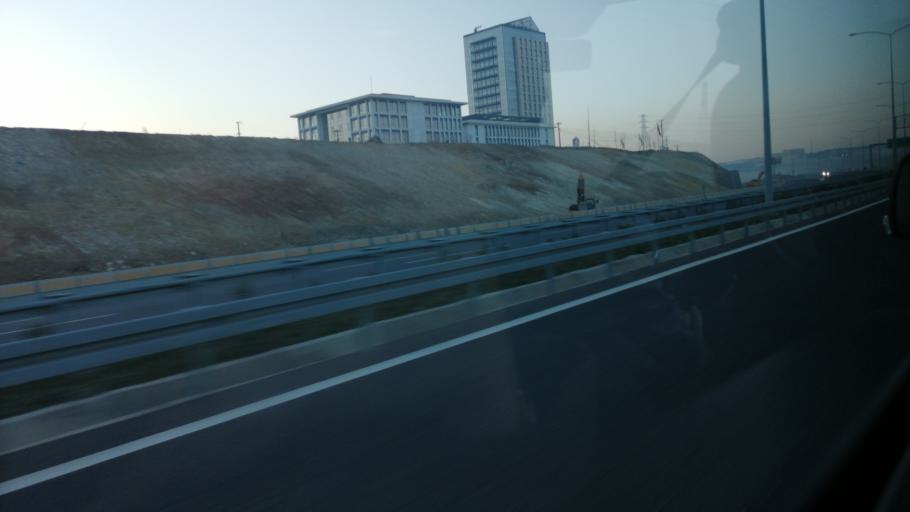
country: TR
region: Kocaeli
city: Tavsanli
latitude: 40.7907
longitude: 29.5138
